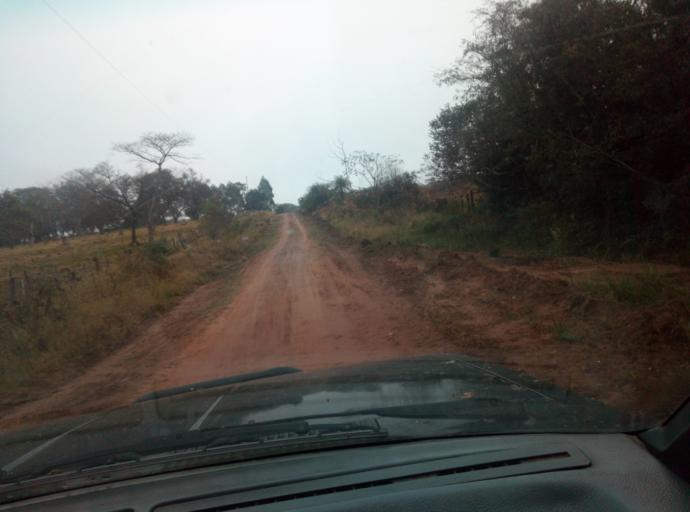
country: PY
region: Caaguazu
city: Carayao
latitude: -25.1904
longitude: -56.3153
